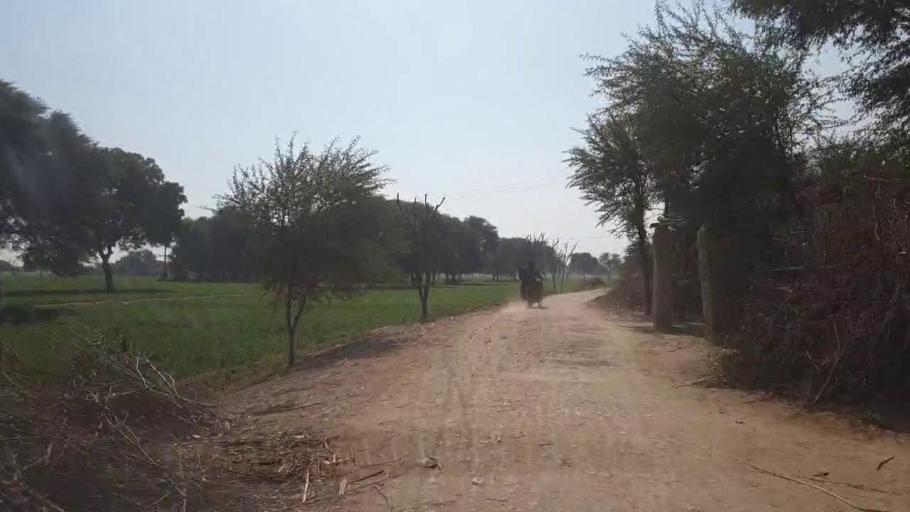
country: PK
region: Sindh
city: Tando Jam
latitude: 25.3025
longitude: 68.6352
